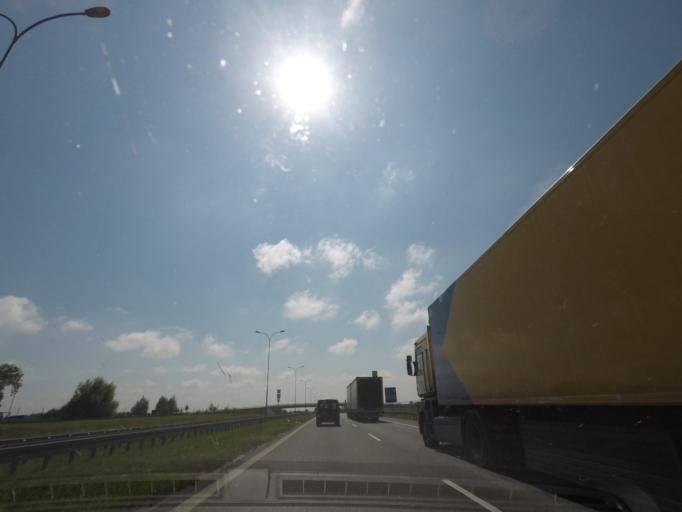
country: PL
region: Kujawsko-Pomorskie
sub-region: Powiat wloclawski
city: Lubien Kujawski
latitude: 52.4690
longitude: 19.1863
